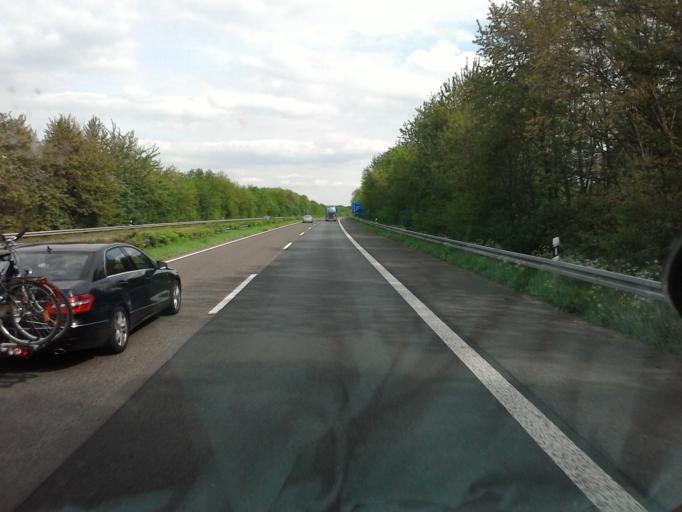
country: DE
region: North Rhine-Westphalia
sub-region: Regierungsbezirk Dusseldorf
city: Uedem
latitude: 51.6428
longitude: 6.2763
